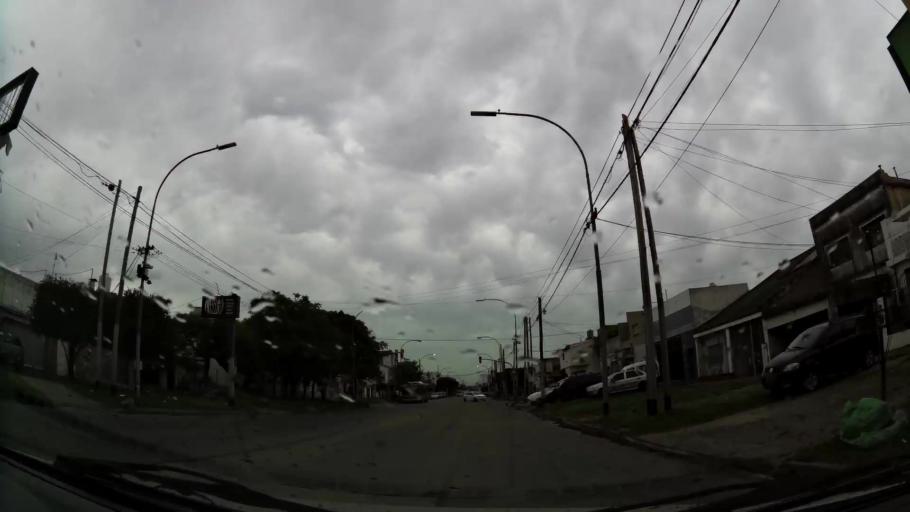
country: AR
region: Buenos Aires
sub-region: Partido de Lanus
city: Lanus
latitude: -34.6871
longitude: -58.3990
